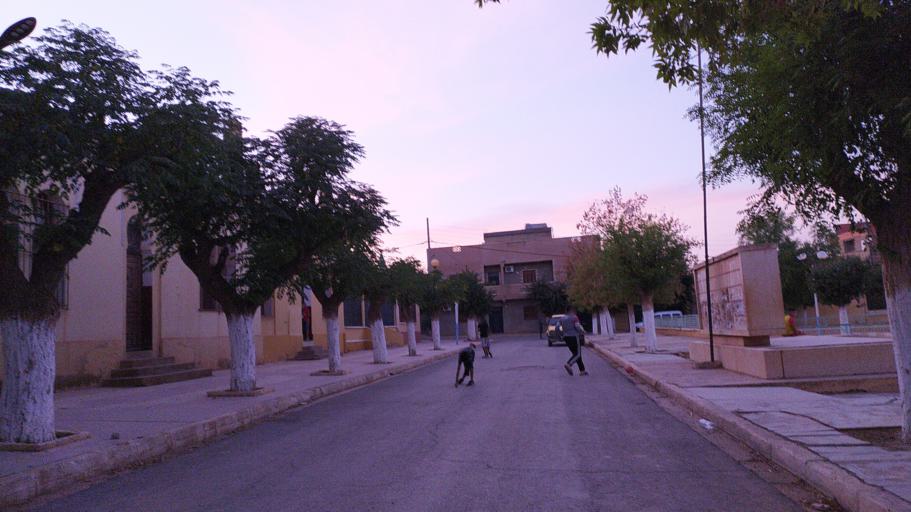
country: DZ
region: Tiaret
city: Frenda
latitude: 34.8959
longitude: 1.2419
